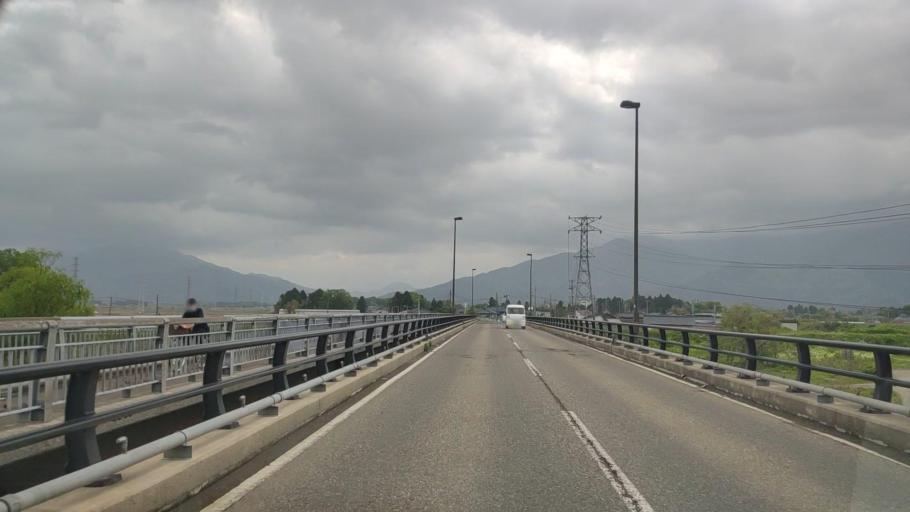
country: JP
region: Niigata
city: Gosen
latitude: 37.7326
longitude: 139.2027
